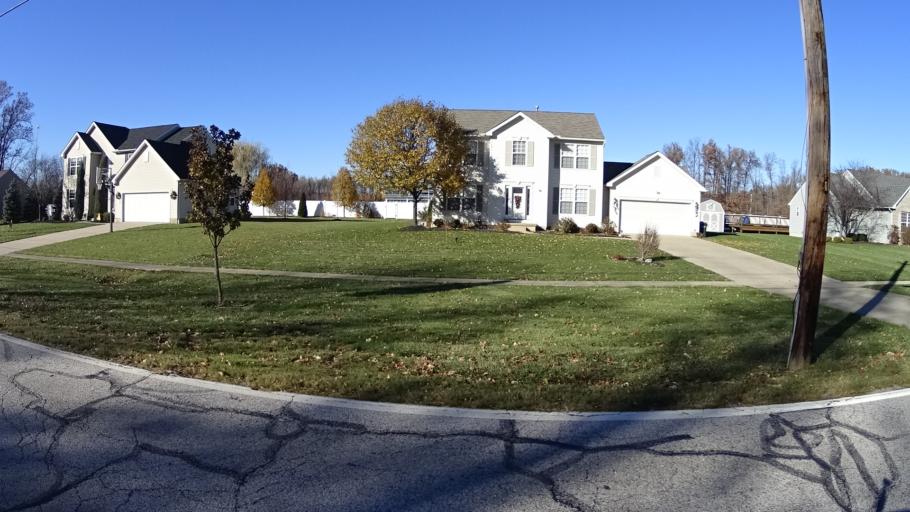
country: US
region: Ohio
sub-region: Lorain County
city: Avon Center
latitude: 41.4663
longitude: -81.9805
